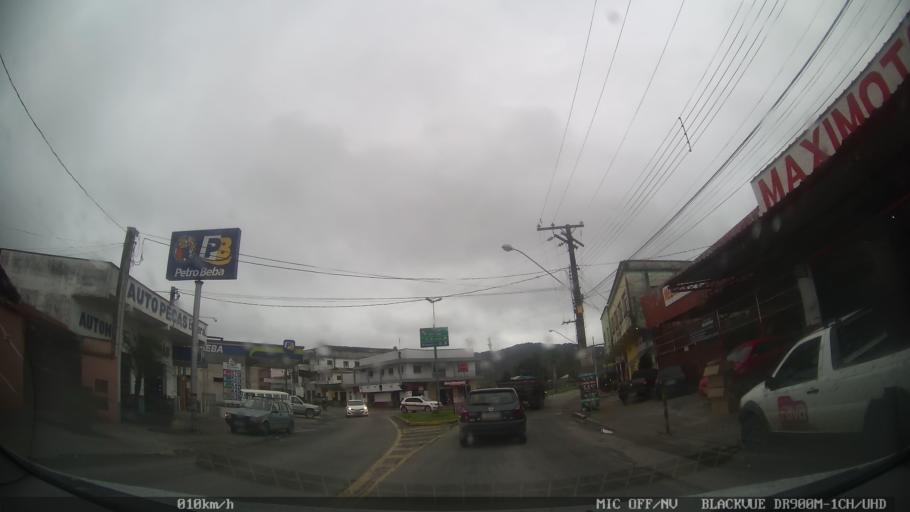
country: BR
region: Sao Paulo
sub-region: Juquia
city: Juquia
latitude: -24.3271
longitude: -47.6315
